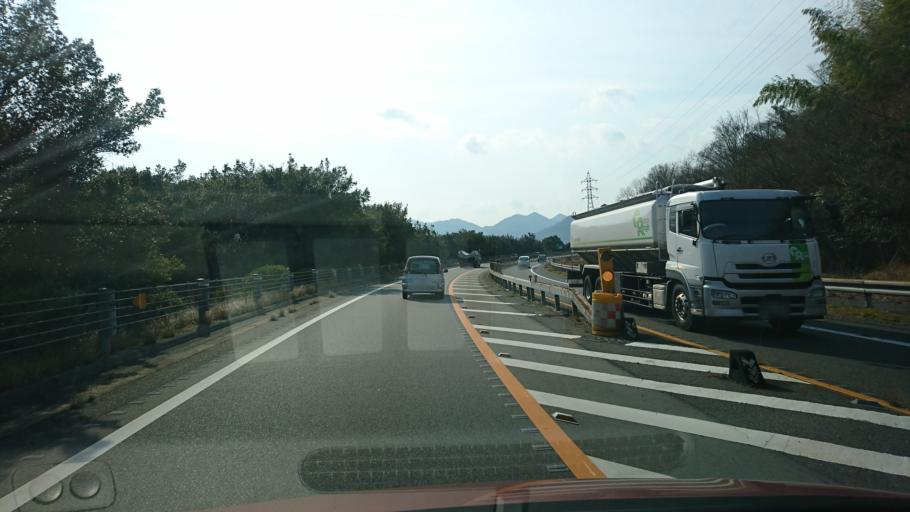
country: JP
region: Hiroshima
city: Onomichi
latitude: 34.3639
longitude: 133.1921
